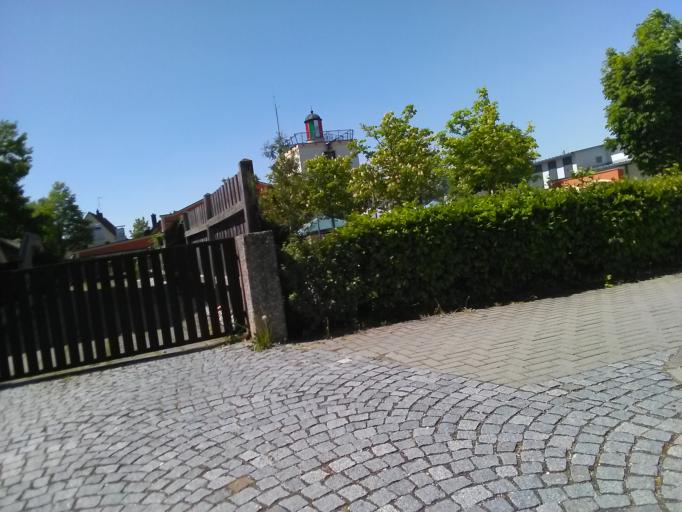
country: DE
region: Bavaria
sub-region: Regierungsbezirk Mittelfranken
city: Gunzenhausen
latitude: 49.1215
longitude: 10.7532
